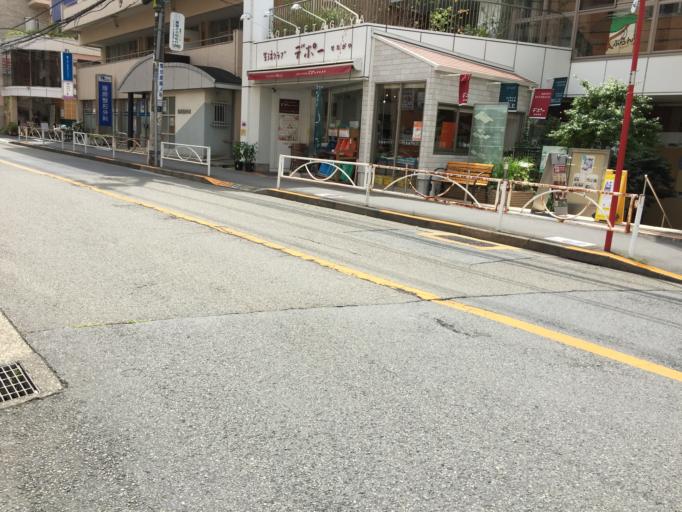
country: JP
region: Tokyo
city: Tokyo
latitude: 35.6529
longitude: 139.6377
